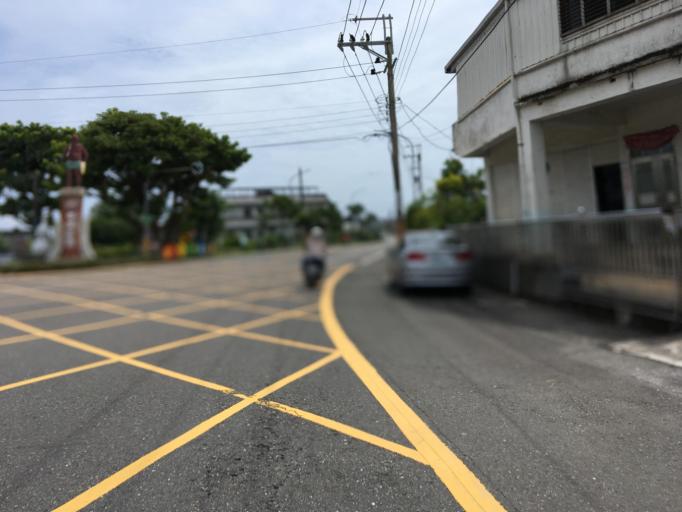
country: TW
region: Taiwan
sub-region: Yilan
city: Yilan
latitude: 24.6934
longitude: 121.8079
